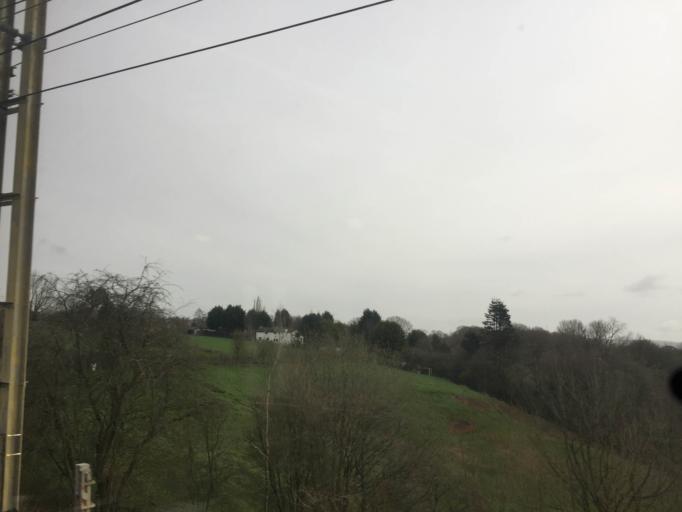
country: GB
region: England
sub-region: Lancashire
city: Coppull
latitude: 53.6326
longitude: -2.6629
